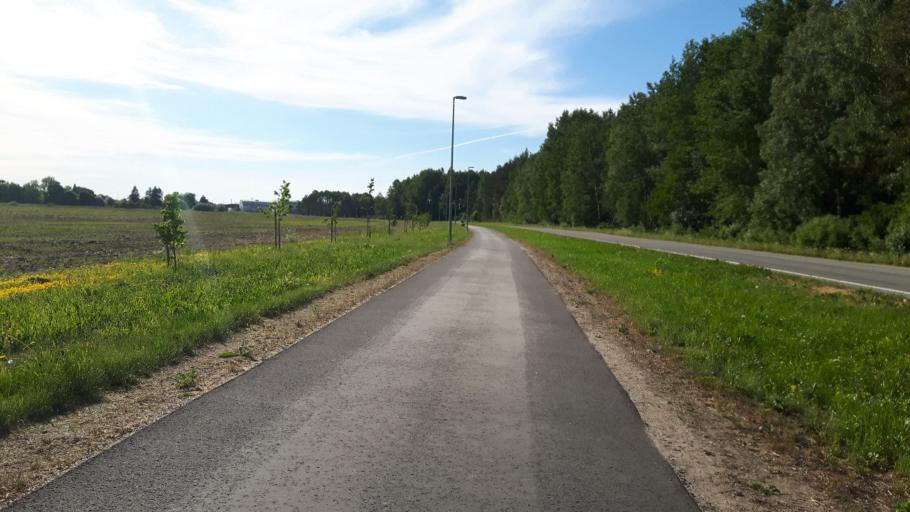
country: EE
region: Harju
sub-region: Joelaehtme vald
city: Loo
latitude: 59.4294
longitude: 24.9812
